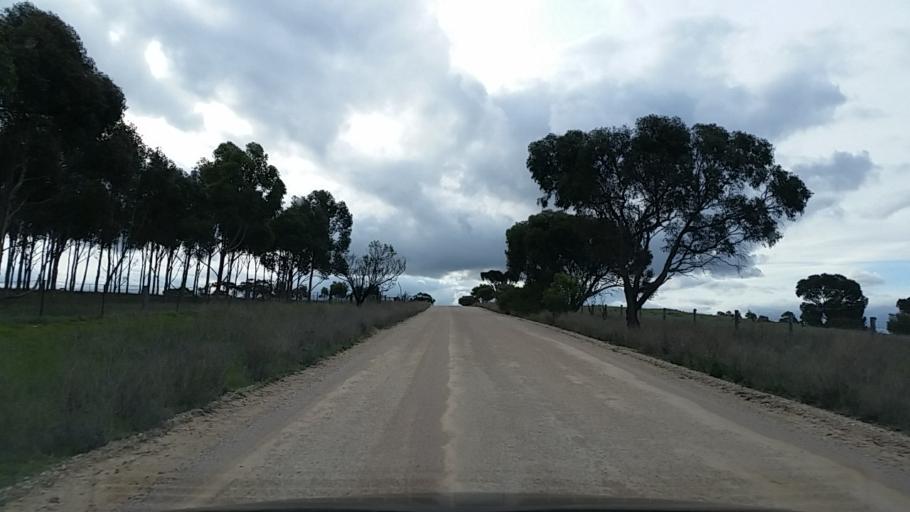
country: AU
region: South Australia
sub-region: Mount Barker
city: Callington
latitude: -35.0087
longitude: 139.0628
